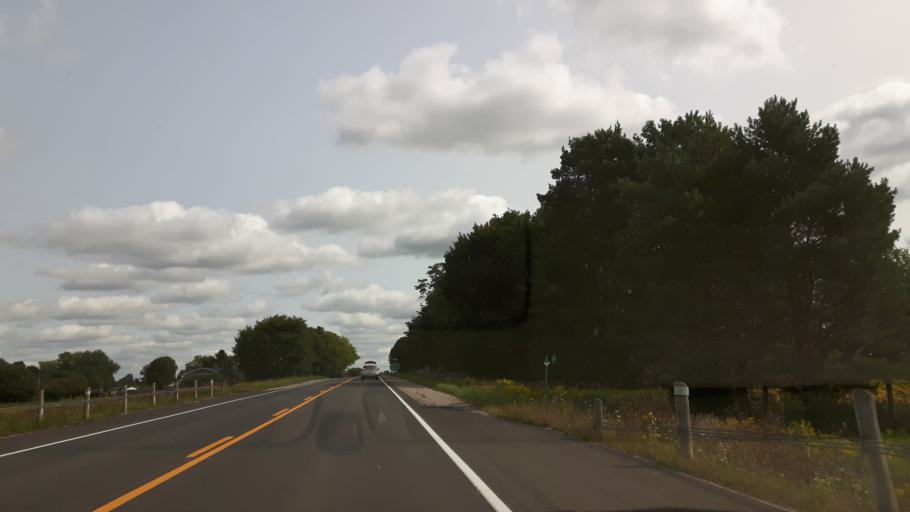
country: CA
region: Ontario
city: Huron East
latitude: 43.5842
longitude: -81.4638
